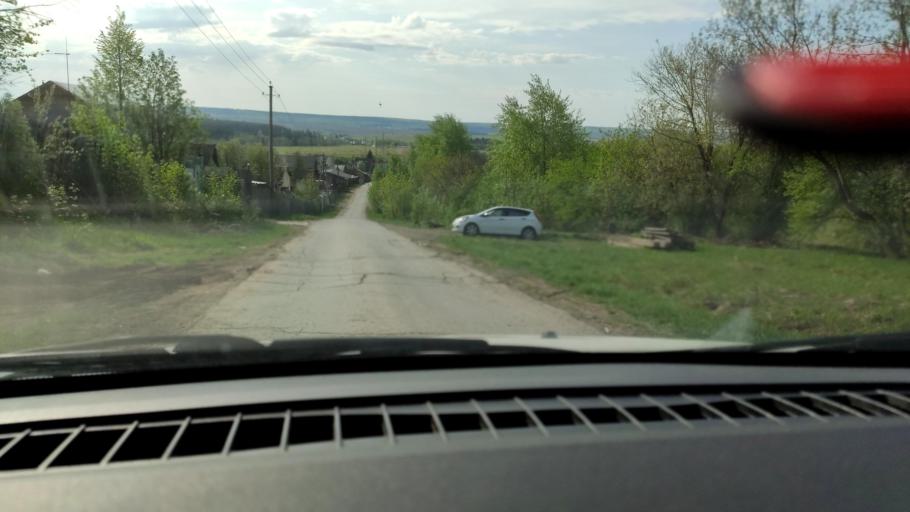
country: RU
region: Perm
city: Froly
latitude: 57.9478
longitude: 56.2971
